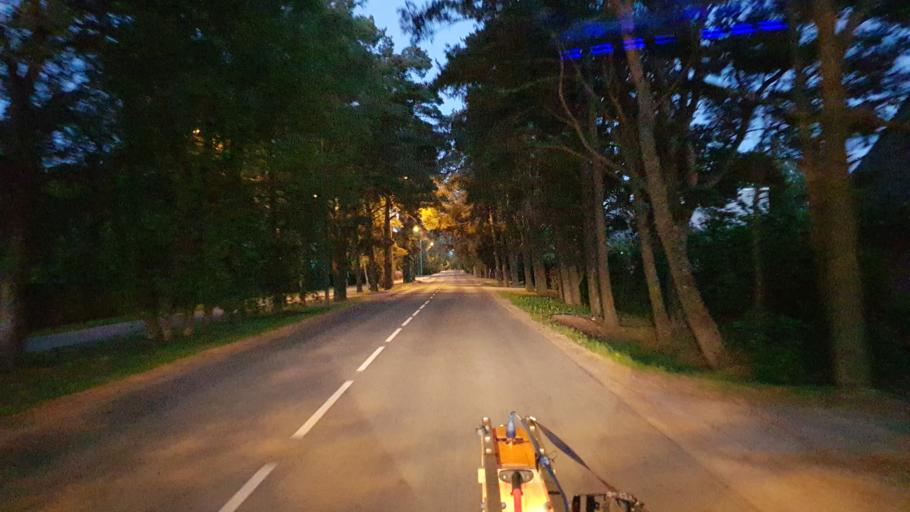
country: EE
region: Harju
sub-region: Harku vald
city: Tabasalu
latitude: 59.4421
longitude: 24.5949
